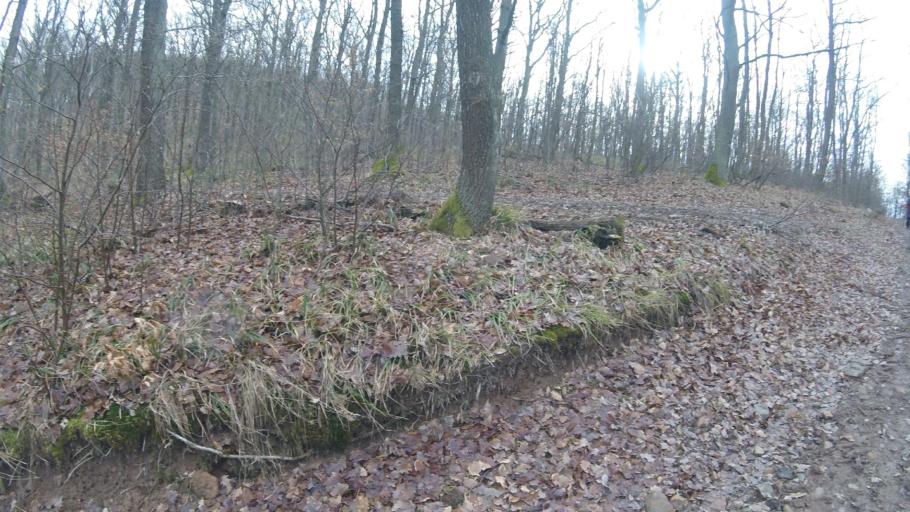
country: HU
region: Pest
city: Csobanka
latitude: 47.6949
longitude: 18.9586
